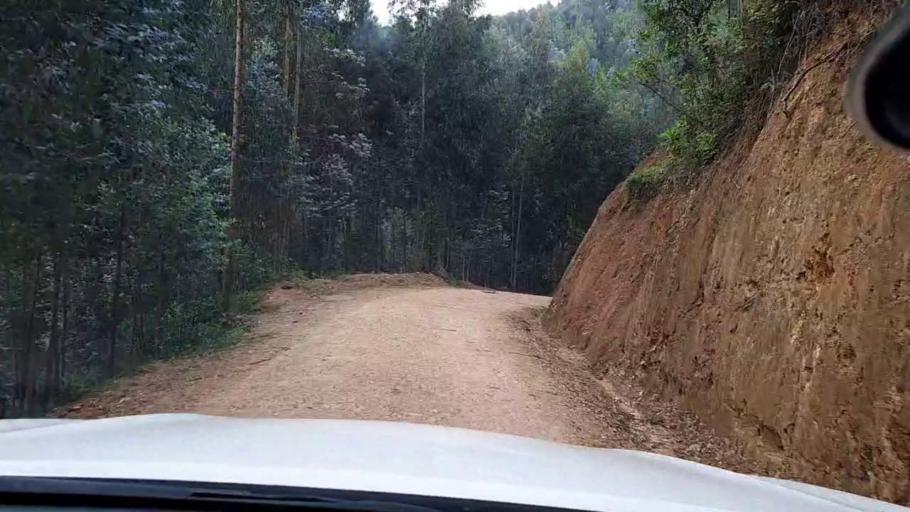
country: RW
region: Western Province
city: Kibuye
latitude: -2.2805
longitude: 29.3016
